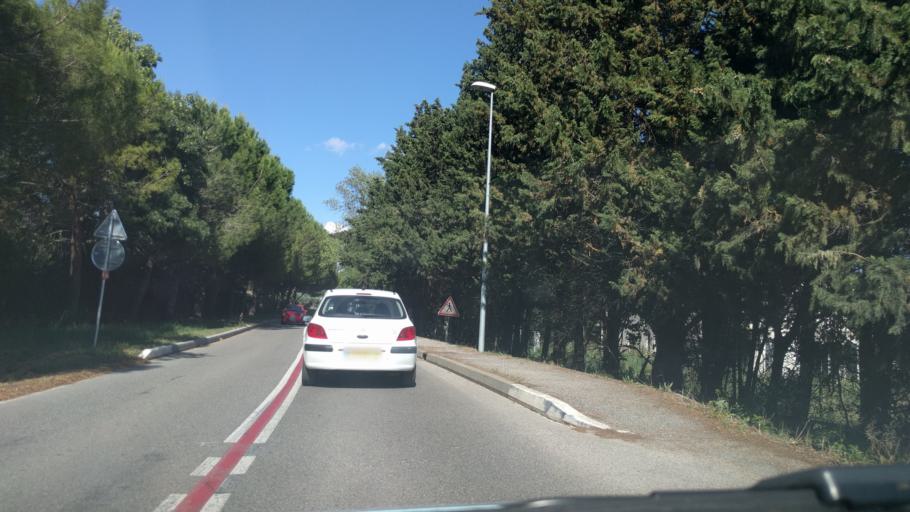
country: FR
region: Provence-Alpes-Cote d'Azur
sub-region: Departement des Bouches-du-Rhone
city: Eguilles
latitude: 43.5246
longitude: 5.3923
